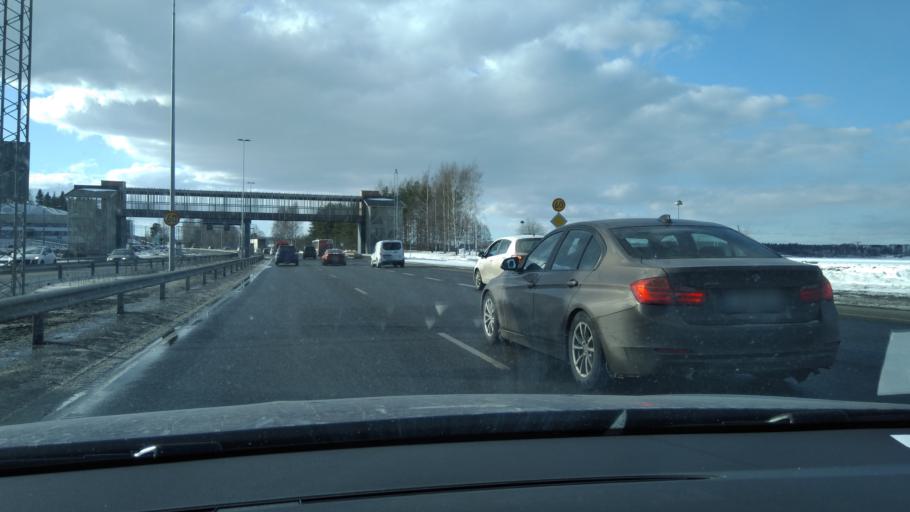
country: FI
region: Pirkanmaa
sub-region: Tampere
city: Tampere
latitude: 61.5056
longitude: 23.7167
